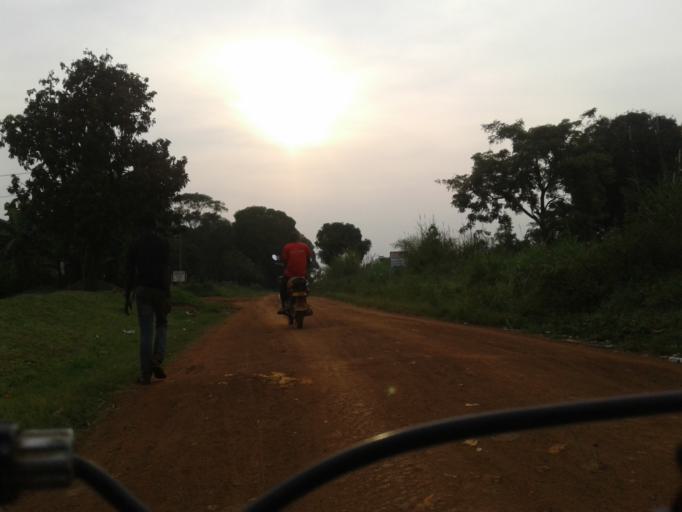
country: UG
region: Western Region
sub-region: Hoima District
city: Hoima
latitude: 1.4236
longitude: 31.3232
